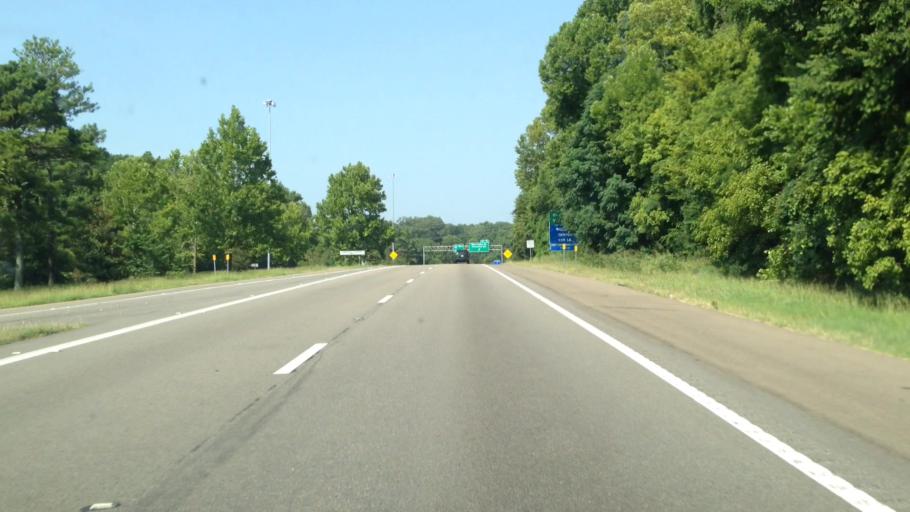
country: US
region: Mississippi
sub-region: Warren County
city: Vicksburg
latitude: 32.3120
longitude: -90.8916
